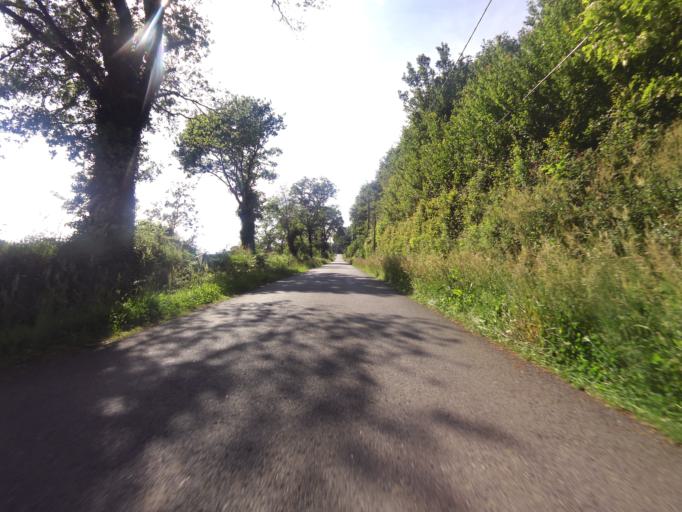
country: FR
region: Brittany
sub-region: Departement du Morbihan
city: Pluherlin
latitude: 47.7059
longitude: -2.3641
